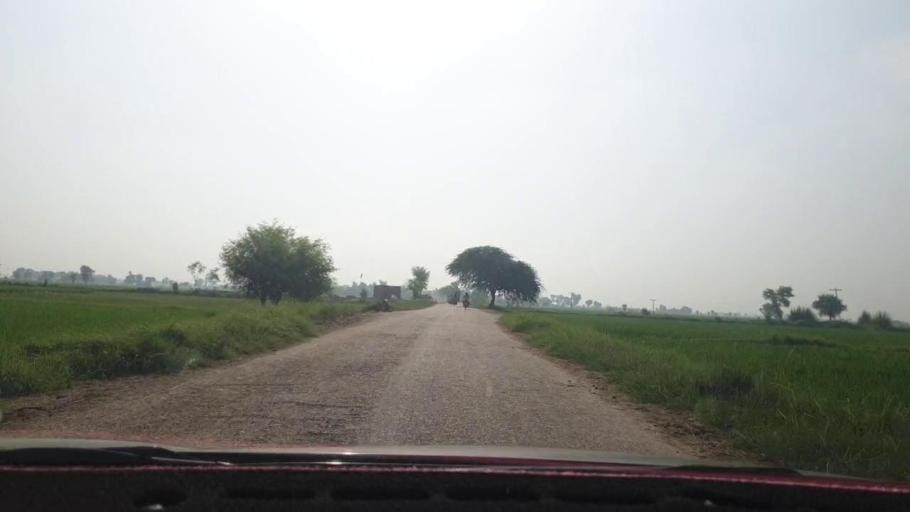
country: PK
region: Sindh
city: Nasirabad
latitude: 27.4416
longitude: 67.9484
